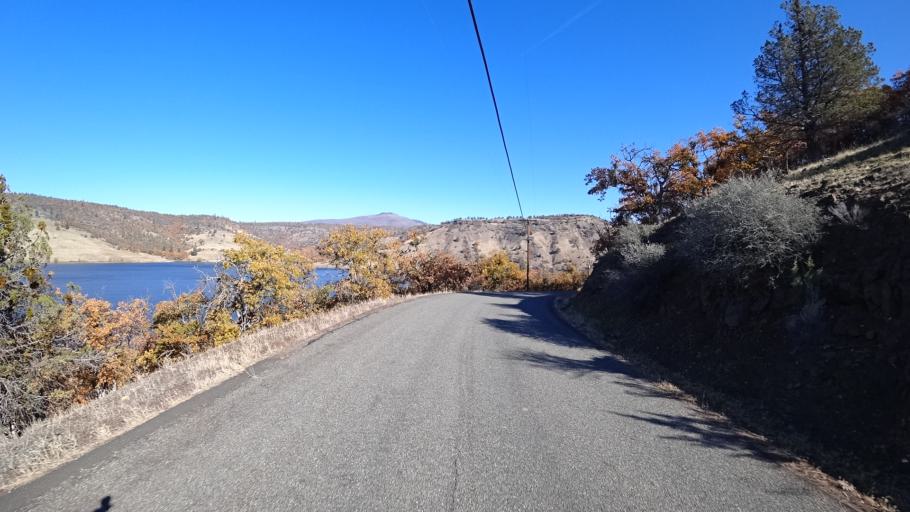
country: US
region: California
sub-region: Siskiyou County
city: Montague
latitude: 41.9800
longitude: -122.3118
